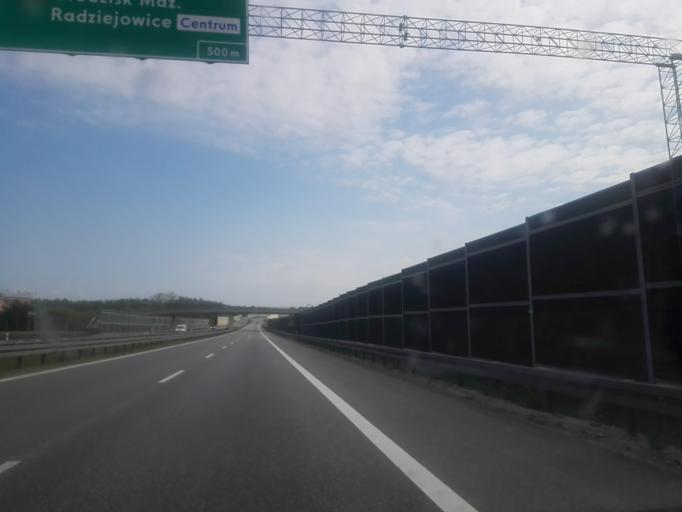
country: PL
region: Masovian Voivodeship
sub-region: Powiat zyrardowski
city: Radziejowice
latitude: 51.9950
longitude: 20.5490
